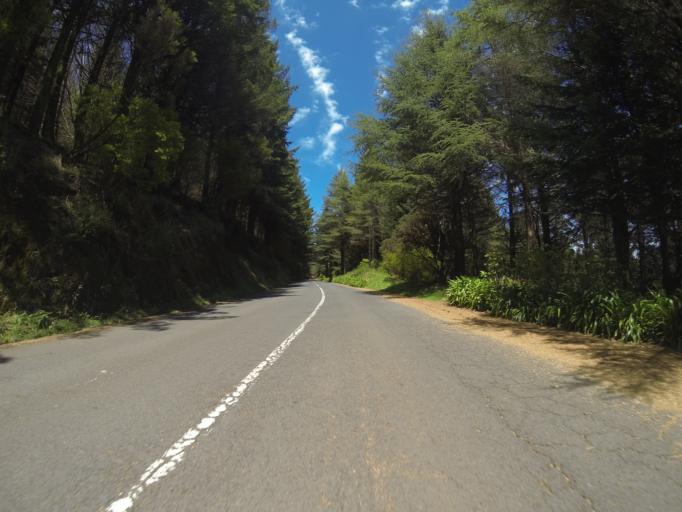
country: PT
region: Madeira
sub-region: Funchal
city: Nossa Senhora do Monte
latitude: 32.7119
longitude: -16.8898
